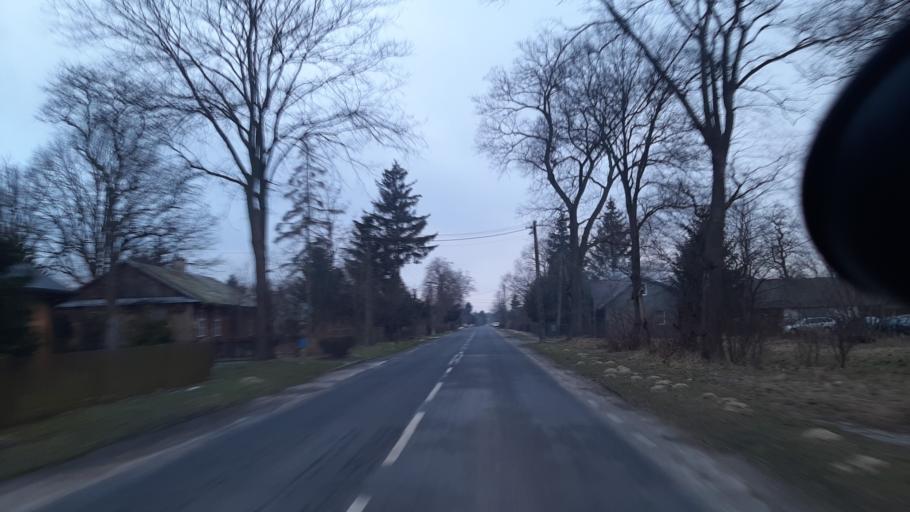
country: PL
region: Lublin Voivodeship
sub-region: Powiat parczewski
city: Debowa Kloda
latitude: 51.6373
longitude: 23.0457
